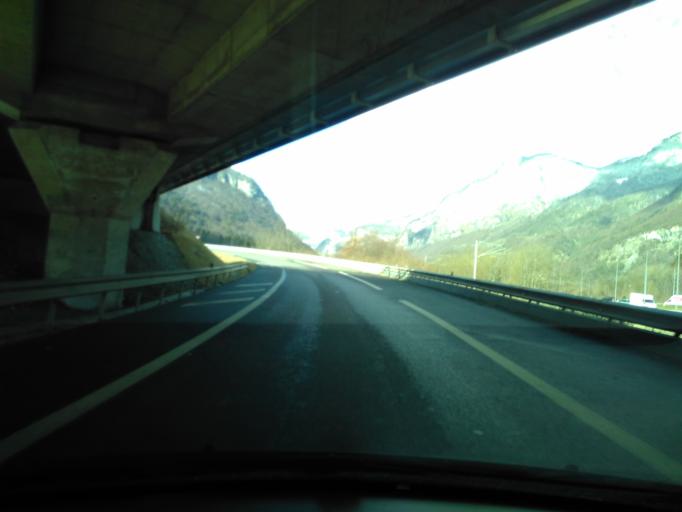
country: FR
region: Rhone-Alpes
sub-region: Departement de la Haute-Savoie
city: Sallanches
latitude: 45.9636
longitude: 6.6295
